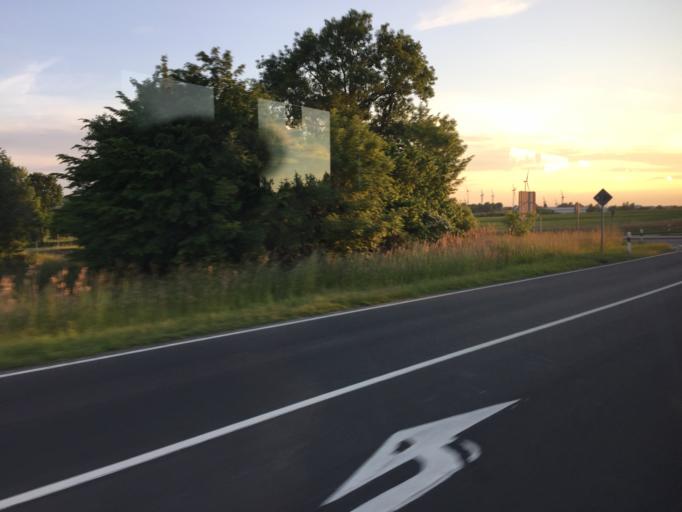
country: DE
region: Saxony
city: Reichenbach
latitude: 51.1483
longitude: 14.8081
